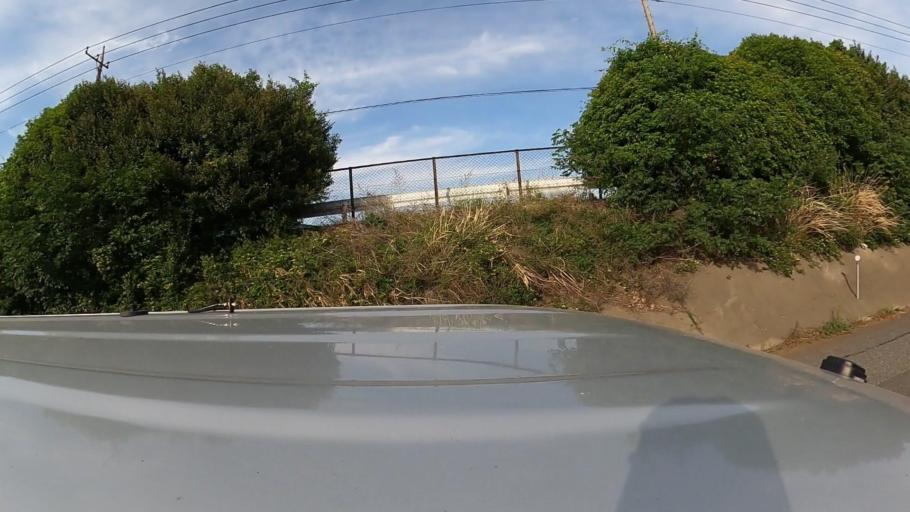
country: JP
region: Saitama
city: Oi
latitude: 35.8137
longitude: 139.5268
